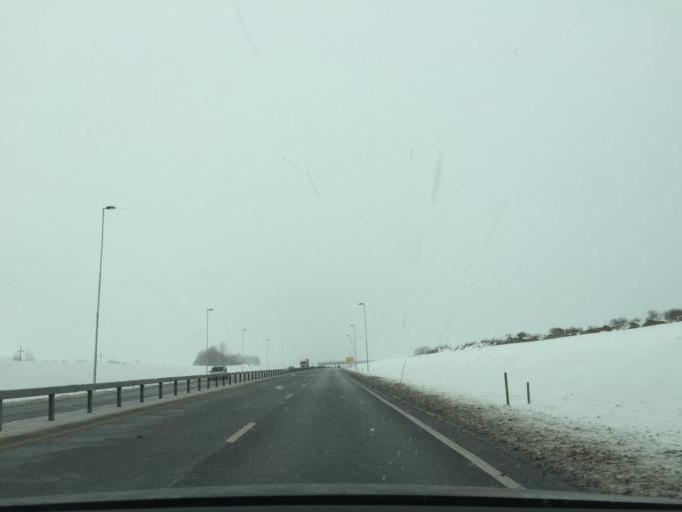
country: NO
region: Hedmark
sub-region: Kongsvinger
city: Spetalen
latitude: 60.2334
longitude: 11.8317
